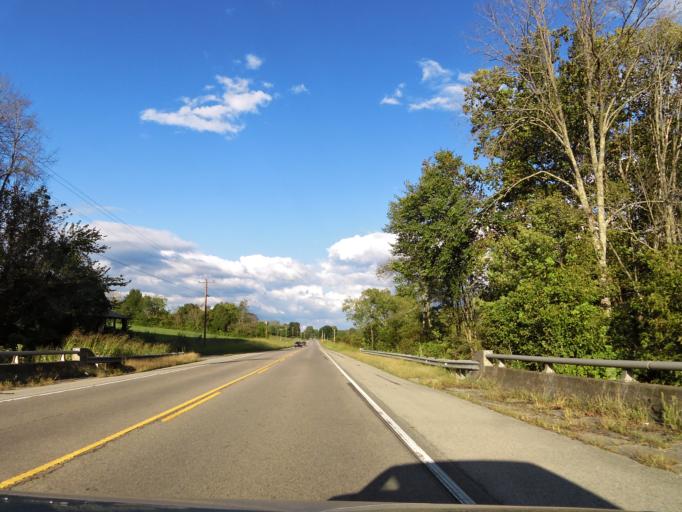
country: US
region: Tennessee
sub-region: Grainger County
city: Rutledge
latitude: 36.2513
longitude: -83.5896
